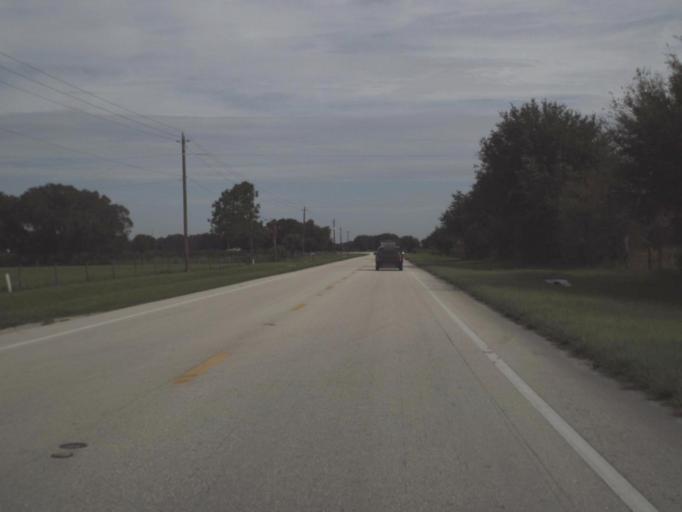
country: US
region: Florida
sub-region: DeSoto County
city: Southeast Arcadia
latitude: 27.1156
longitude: -81.7947
